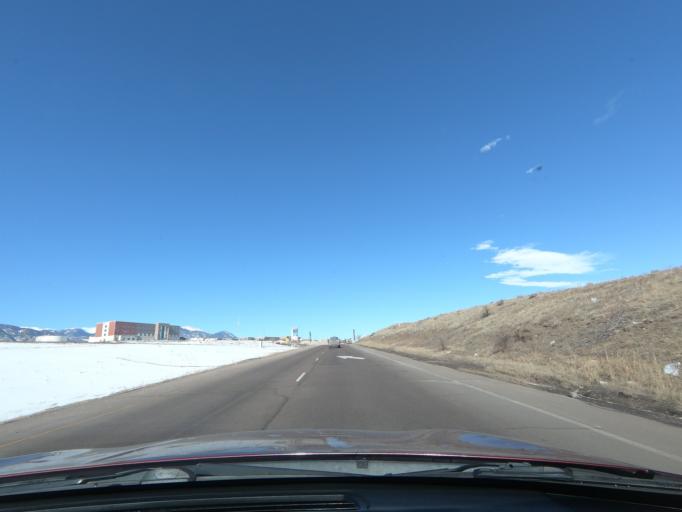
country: US
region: Colorado
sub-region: El Paso County
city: Stratmoor
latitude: 38.7668
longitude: -104.7761
